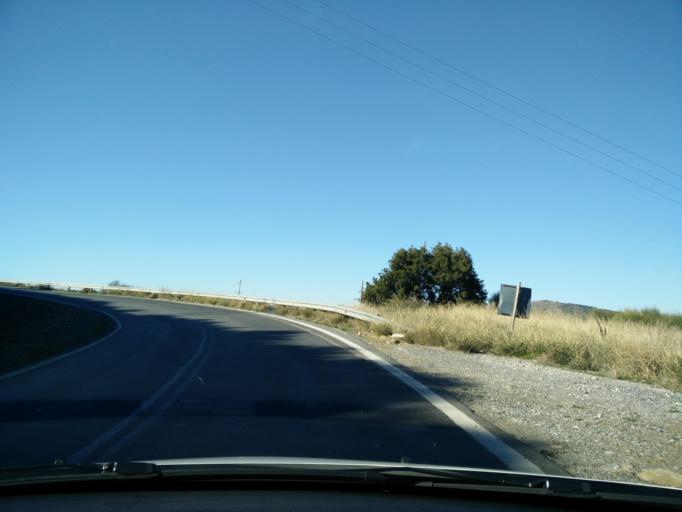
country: GR
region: Crete
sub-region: Nomos Irakleiou
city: Arkalochori
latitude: 35.0693
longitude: 25.3585
